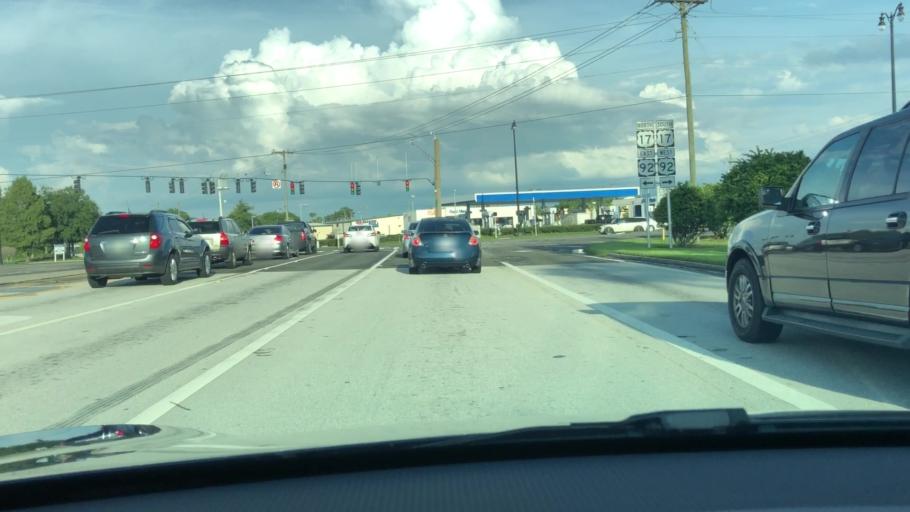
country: US
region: Florida
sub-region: Seminole County
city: Sanford
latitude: 28.7694
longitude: -81.2816
